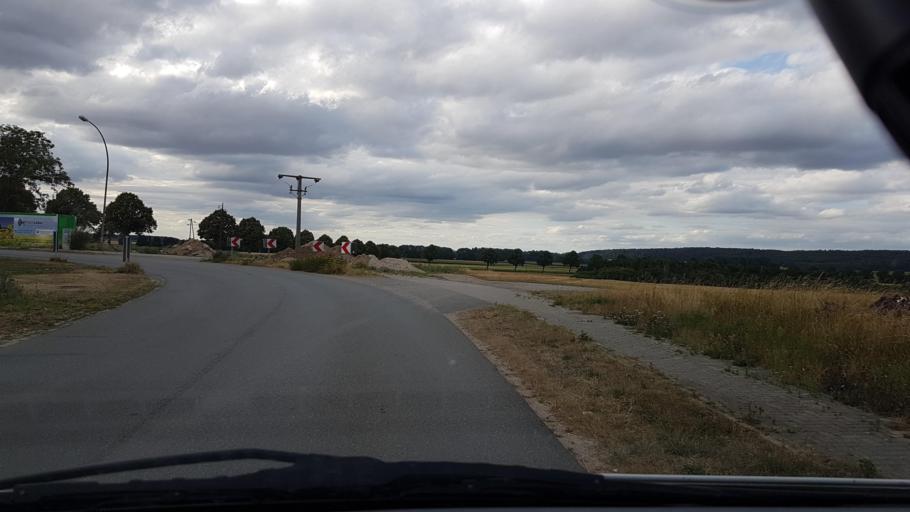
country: DE
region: Lower Saxony
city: Supplingenburg
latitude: 52.2542
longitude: 10.8659
